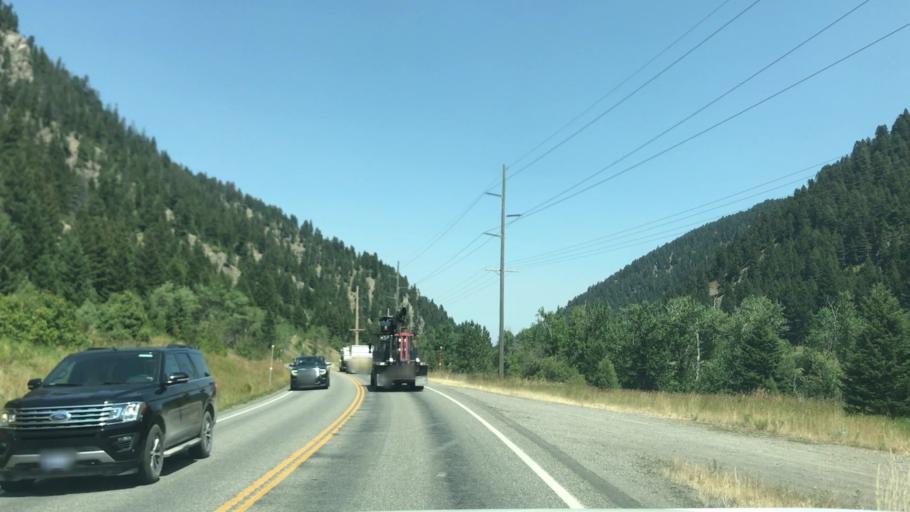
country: US
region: Montana
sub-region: Gallatin County
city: Four Corners
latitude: 45.5027
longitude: -111.2681
